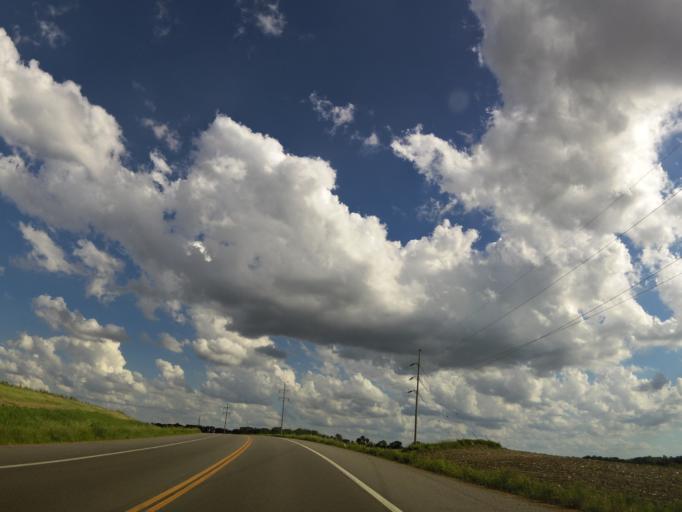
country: US
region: Minnesota
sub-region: Carver County
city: Waconia
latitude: 44.8890
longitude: -93.8186
